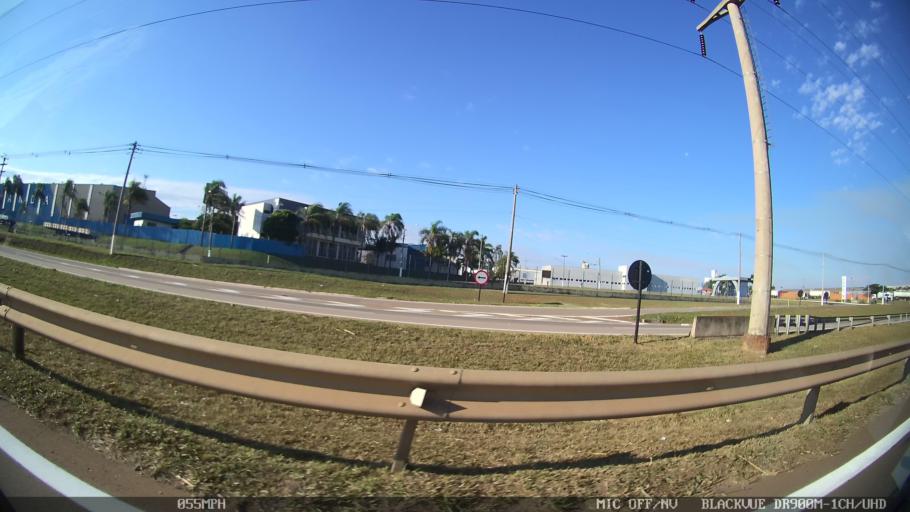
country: BR
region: Sao Paulo
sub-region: Piracicaba
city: Piracicaba
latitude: -22.6639
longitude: -47.6082
